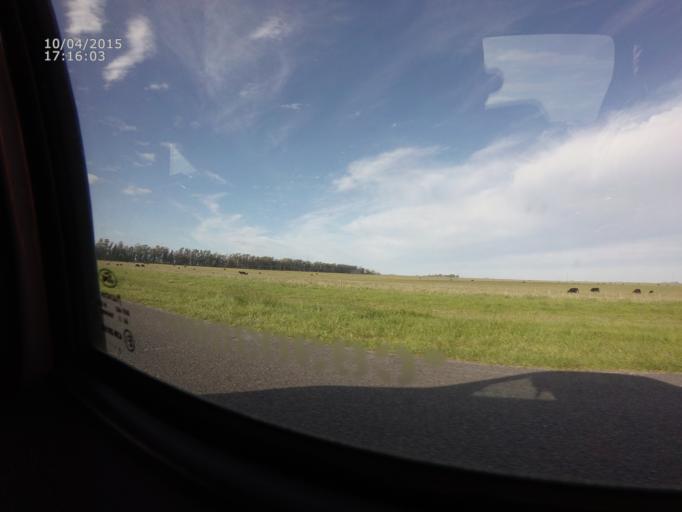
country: AR
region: Buenos Aires
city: Coronel Vidal
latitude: -37.2212
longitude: -57.7933
